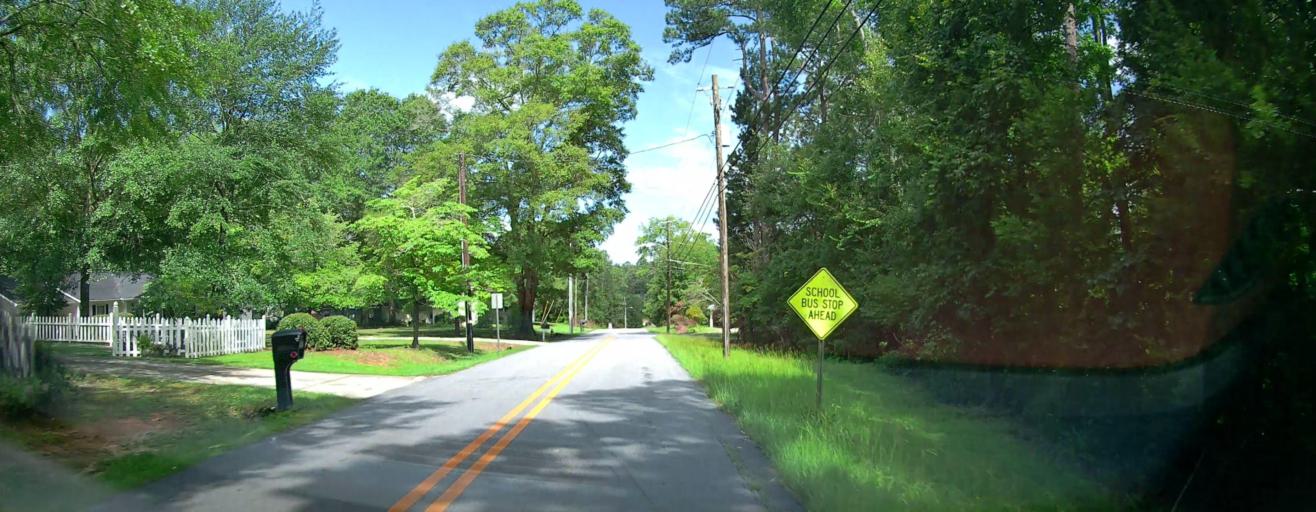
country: US
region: Georgia
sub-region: Peach County
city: Byron
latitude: 32.6561
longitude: -83.7647
